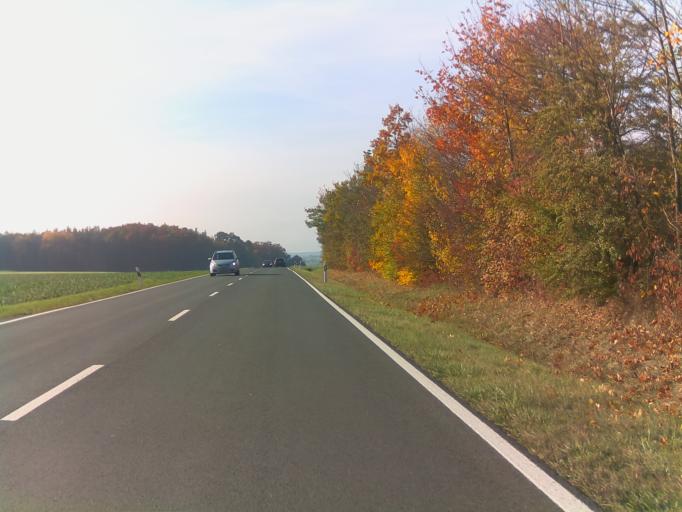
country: DE
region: Bavaria
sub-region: Regierungsbezirk Unterfranken
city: Prichsenstadt
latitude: 49.8467
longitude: 10.3740
